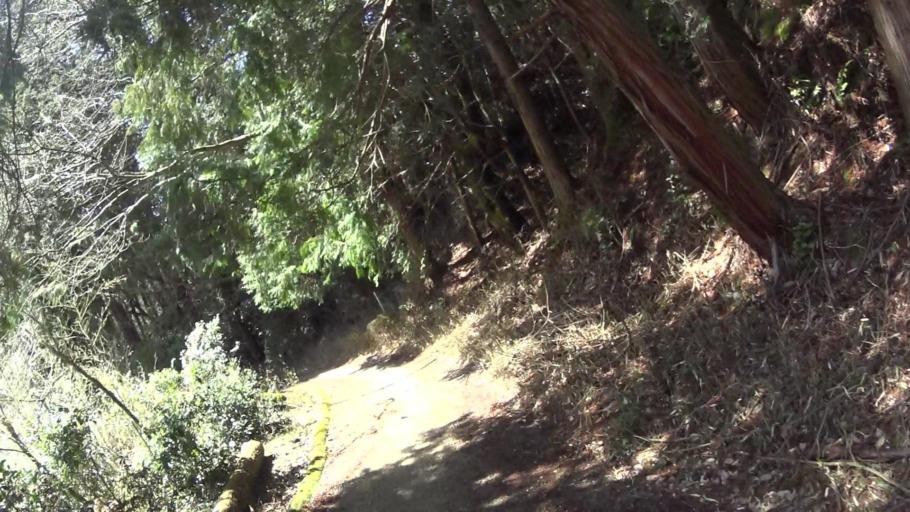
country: JP
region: Shiga Prefecture
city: Otsu-shi
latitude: 35.0035
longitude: 135.8409
